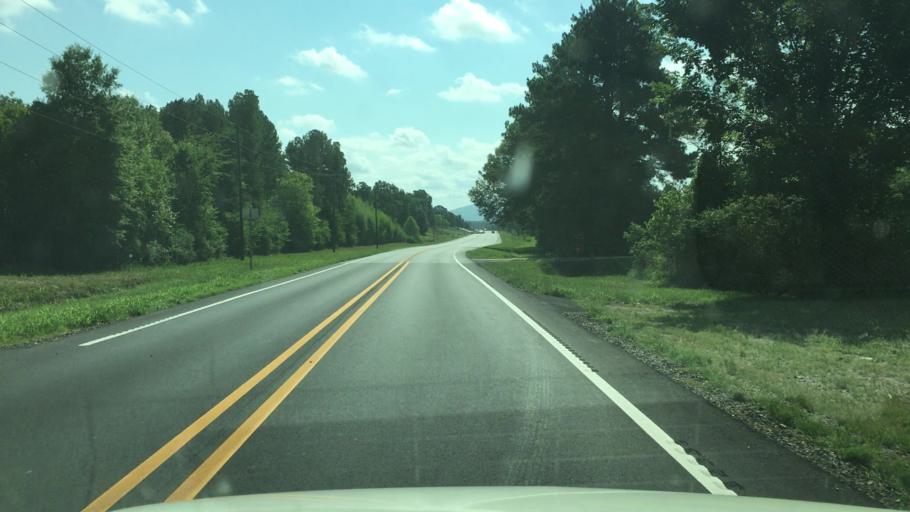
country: US
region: Arkansas
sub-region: Garland County
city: Piney
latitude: 34.5115
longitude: -93.2408
